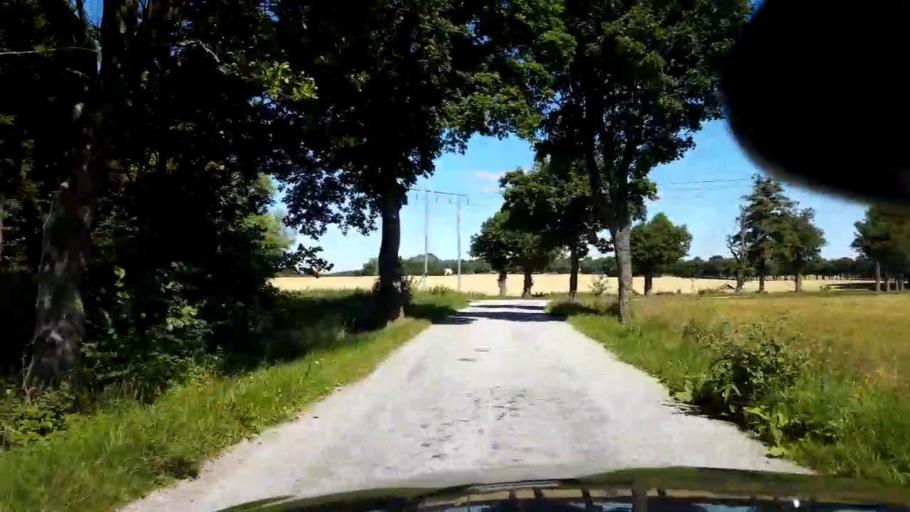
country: SE
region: Stockholm
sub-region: Upplands-Bro Kommun
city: Bro
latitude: 59.5984
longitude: 17.6423
